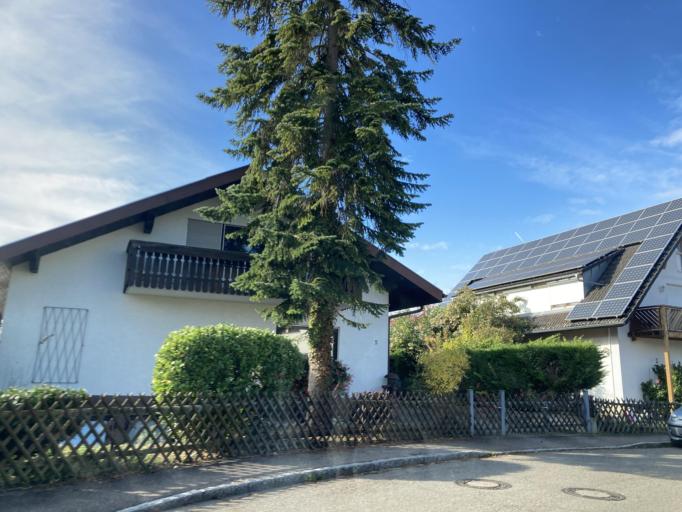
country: DE
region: Baden-Wuerttemberg
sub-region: Freiburg Region
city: Neuenburg am Rhein
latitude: 47.8212
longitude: 7.5661
